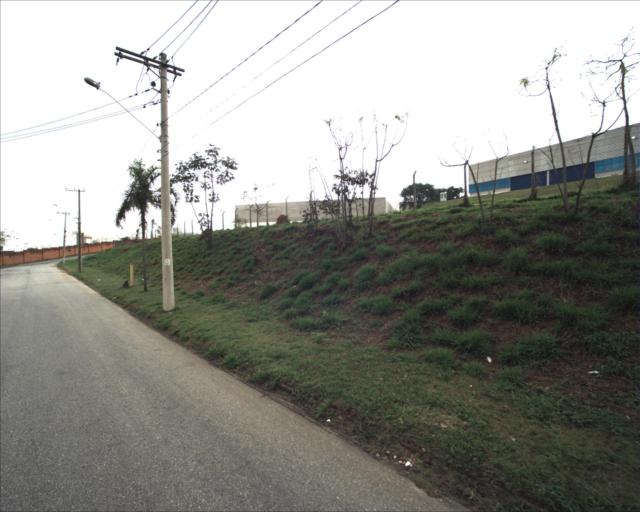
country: BR
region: Sao Paulo
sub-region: Sorocaba
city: Sorocaba
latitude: -23.4463
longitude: -47.4434
